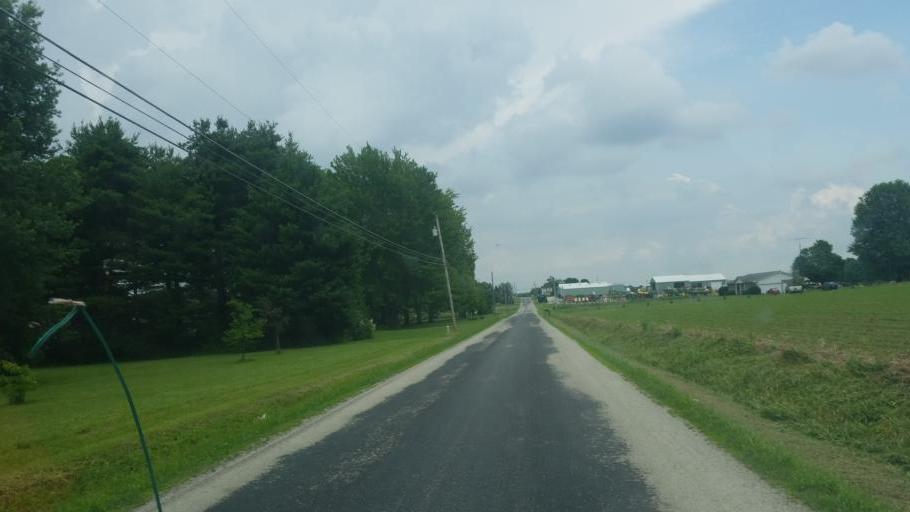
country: US
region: Ohio
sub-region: Wayne County
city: Smithville
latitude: 40.8943
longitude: -81.9225
